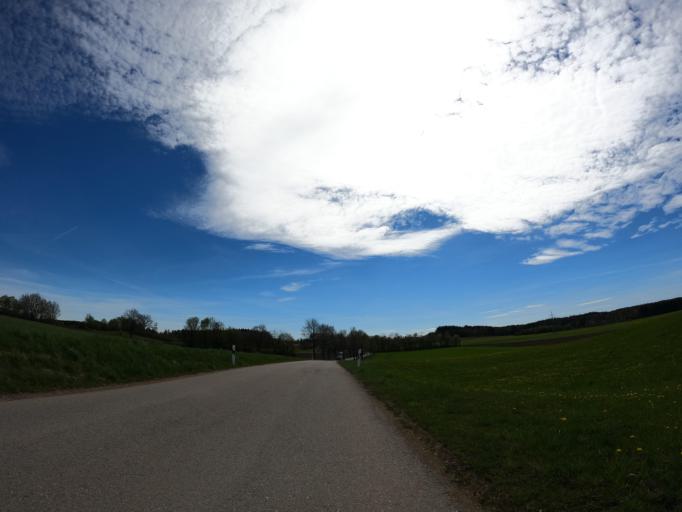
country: DE
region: Bavaria
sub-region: Upper Bavaria
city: Strasslach-Dingharting
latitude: 47.9757
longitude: 11.5183
